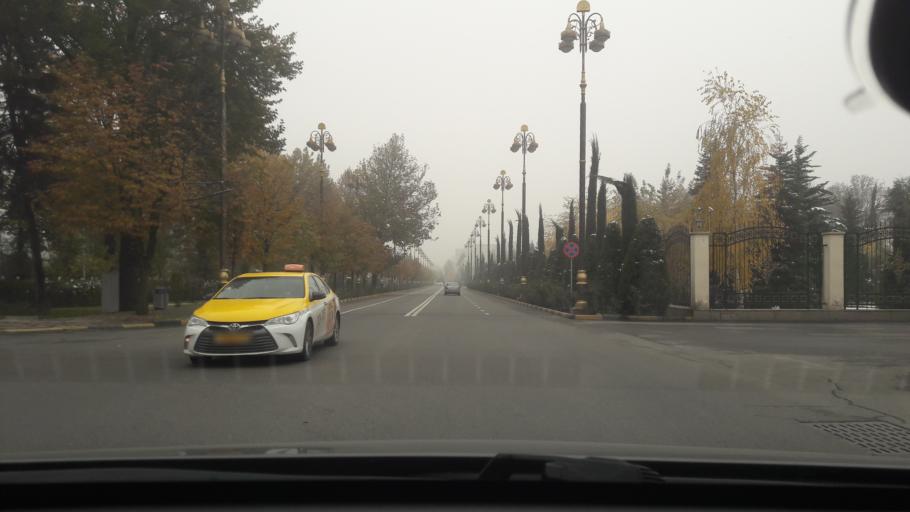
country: TJ
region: Dushanbe
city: Dushanbe
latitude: 38.5783
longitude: 68.7823
